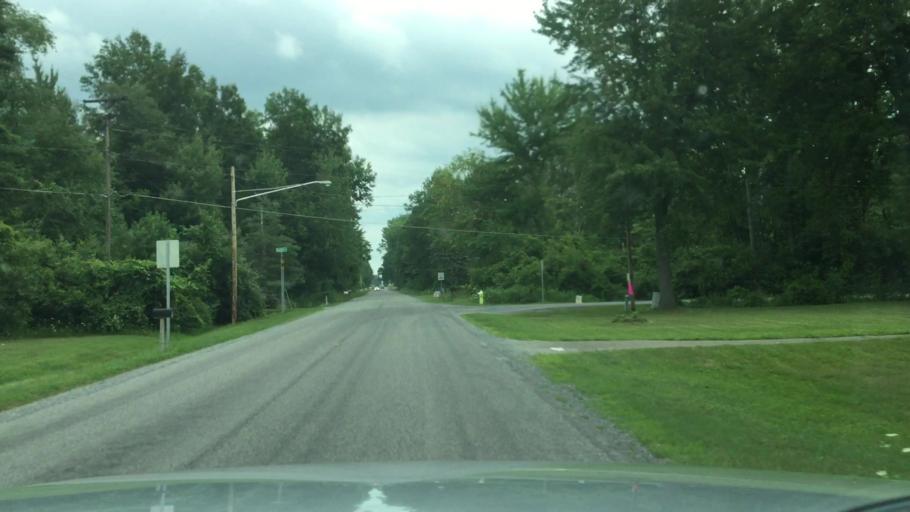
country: US
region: Michigan
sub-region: Saginaw County
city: Bridgeport
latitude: 43.3217
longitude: -83.8752
